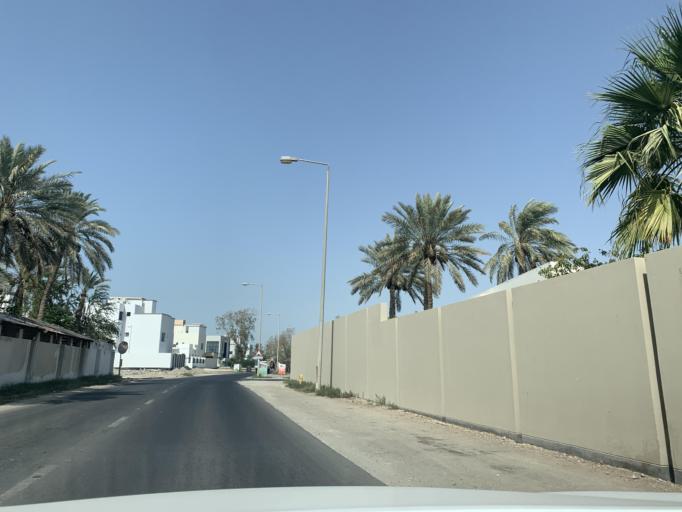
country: BH
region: Manama
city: Jidd Hafs
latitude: 26.2288
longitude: 50.4652
